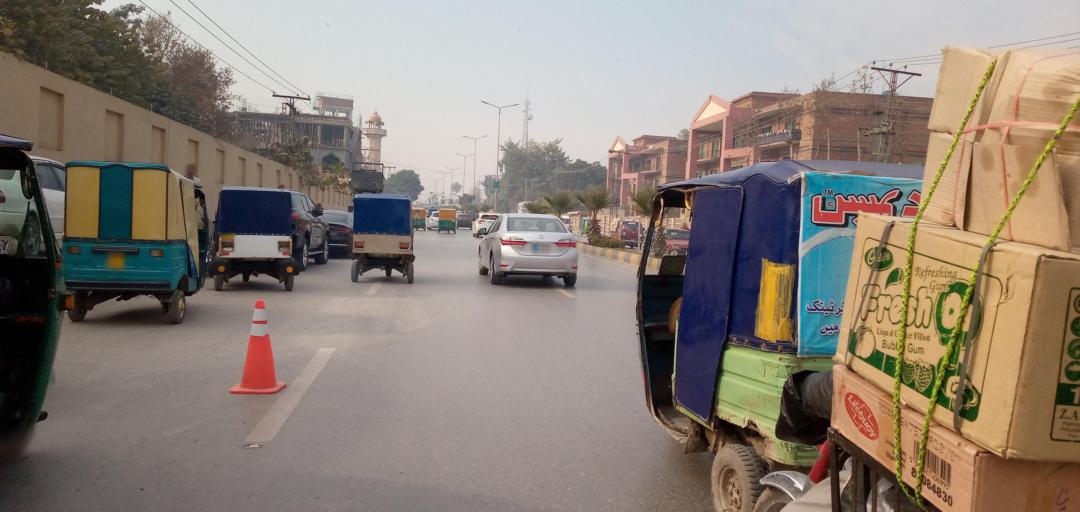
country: PK
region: Khyber Pakhtunkhwa
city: Peshawar
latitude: 34.0145
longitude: 71.5596
